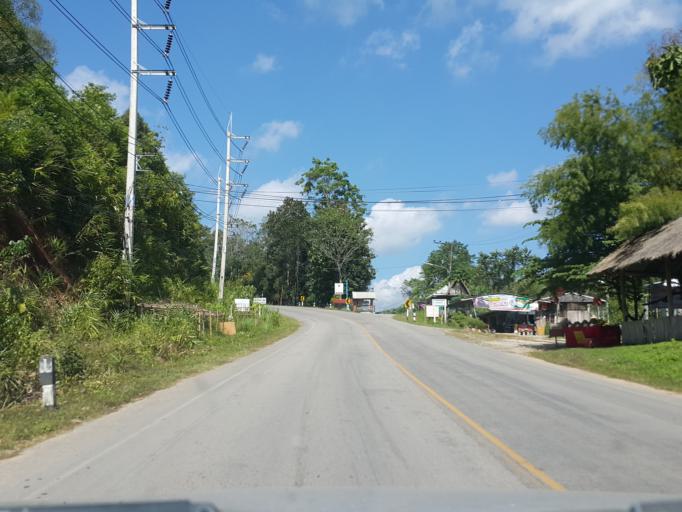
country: TH
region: Chiang Mai
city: Mae Taeng
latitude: 19.1228
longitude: 98.7091
